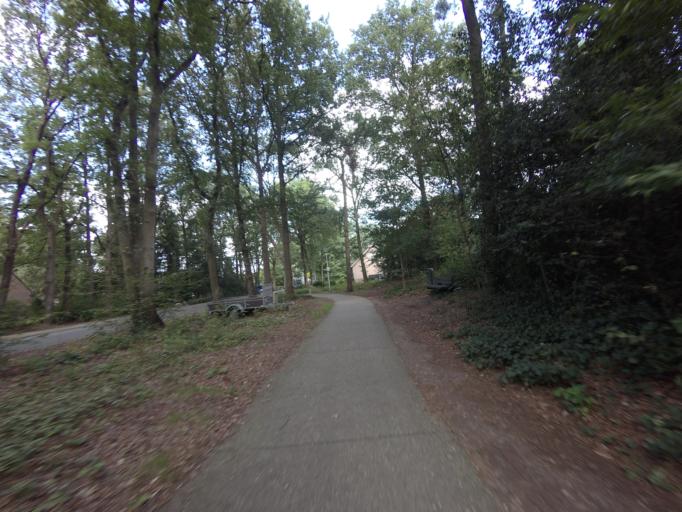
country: NL
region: Overijssel
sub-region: Gemeente Staphorst
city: Staphorst
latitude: 52.6575
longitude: 6.2913
